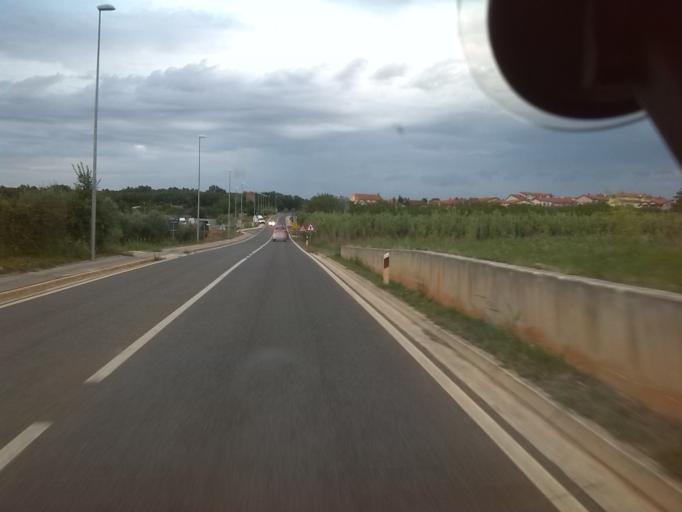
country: HR
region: Istarska
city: Novigrad
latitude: 45.3323
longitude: 13.5777
